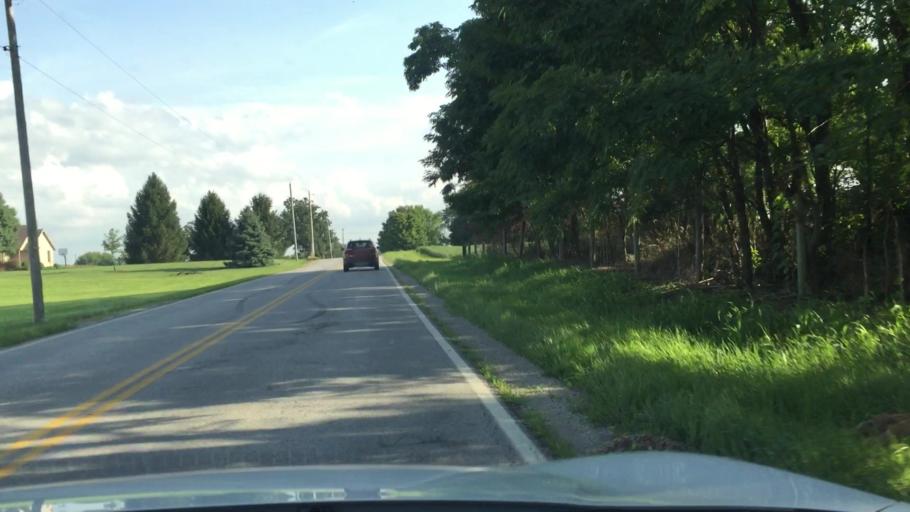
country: US
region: Ohio
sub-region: Clark County
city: Northridge
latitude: 39.9573
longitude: -83.6800
